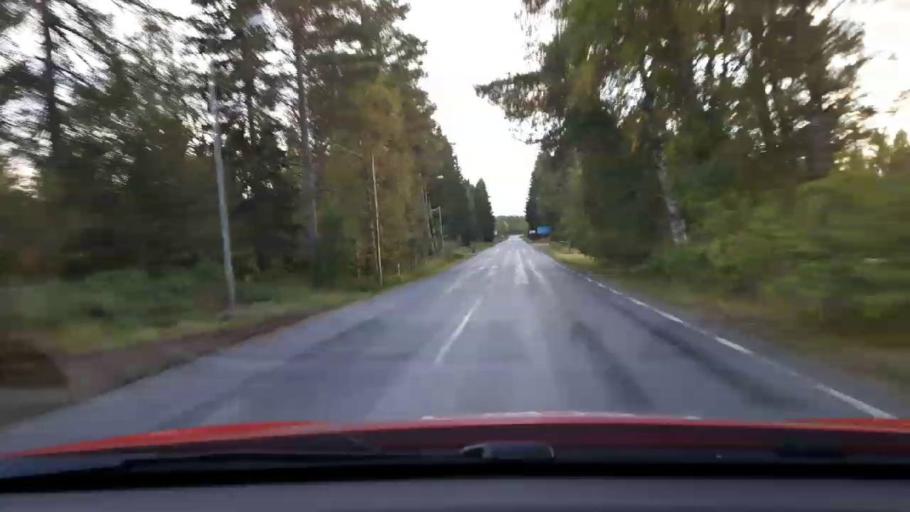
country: SE
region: Jaemtland
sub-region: OEstersunds Kommun
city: Ostersund
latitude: 63.1277
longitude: 14.4479
